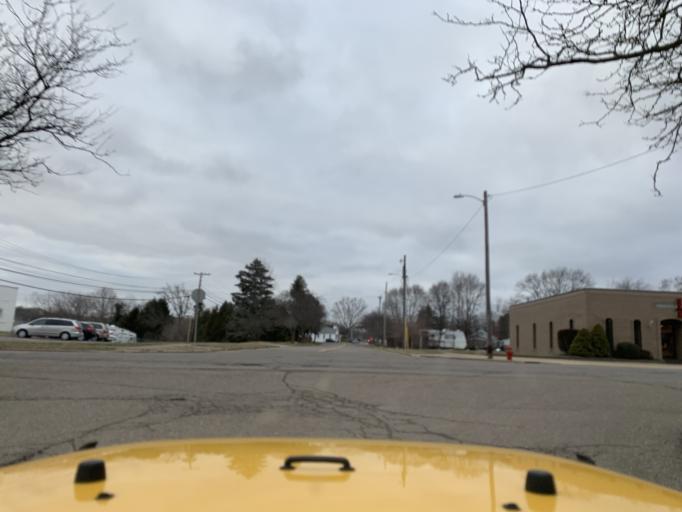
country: US
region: Ohio
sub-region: Tuscarawas County
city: Dover
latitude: 40.5191
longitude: -81.4803
